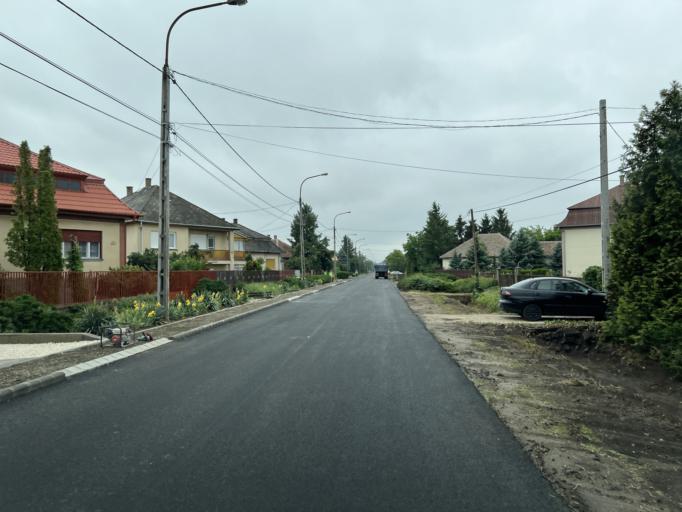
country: HU
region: Pest
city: Tura
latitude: 47.6228
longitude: 19.5970
